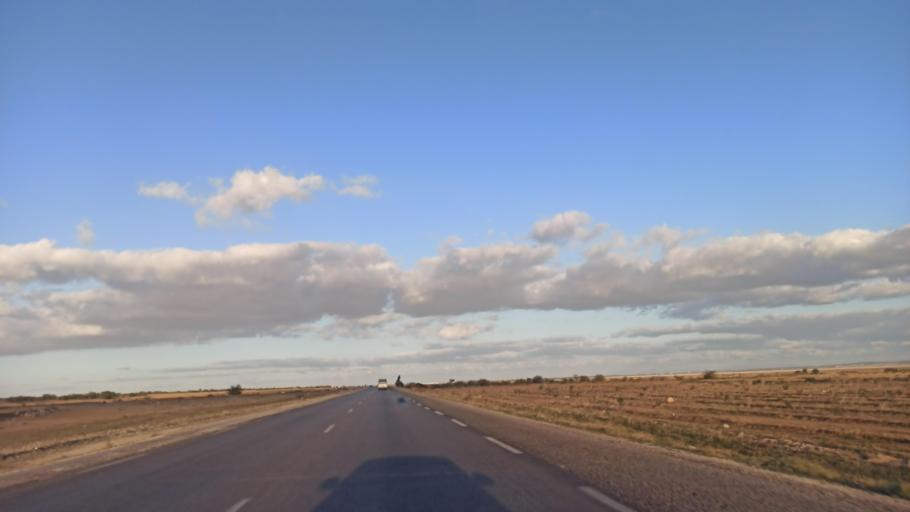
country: TN
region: Susah
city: Sidi el Hani
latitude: 35.8925
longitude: 10.2490
